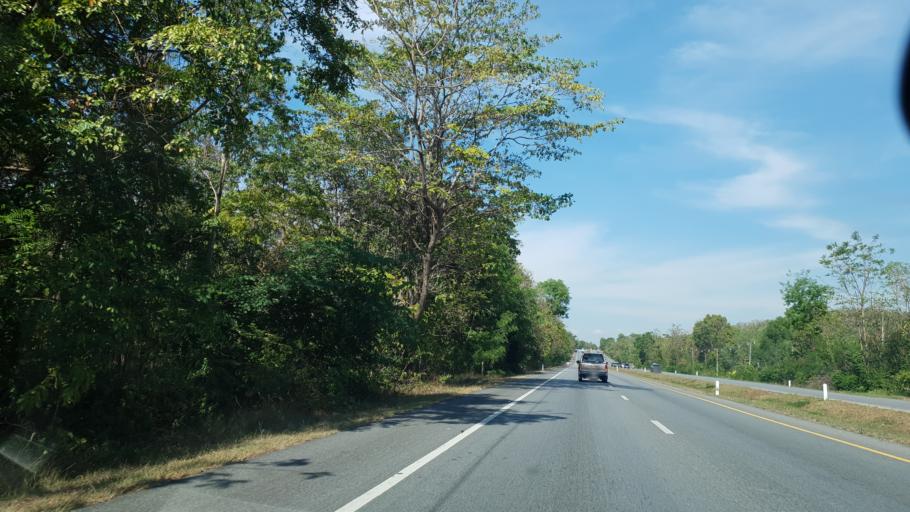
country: TH
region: Uttaradit
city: Thong Saen Khan
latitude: 17.4142
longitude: 100.2280
